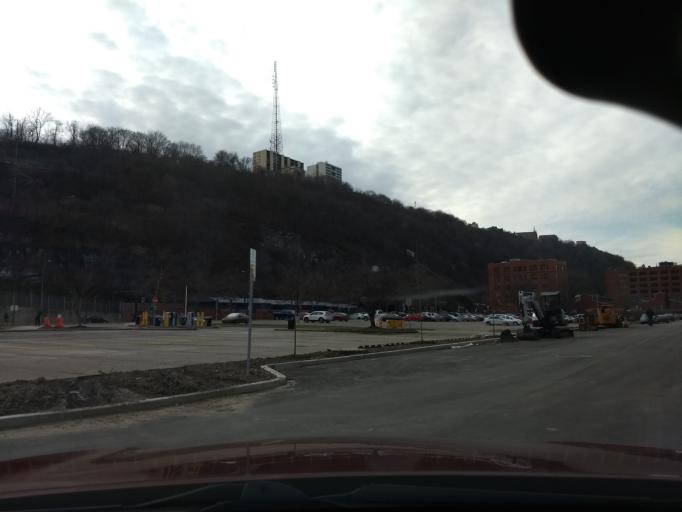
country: US
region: Pennsylvania
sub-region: Allegheny County
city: Pittsburgh
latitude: 40.4318
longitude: -80.0012
